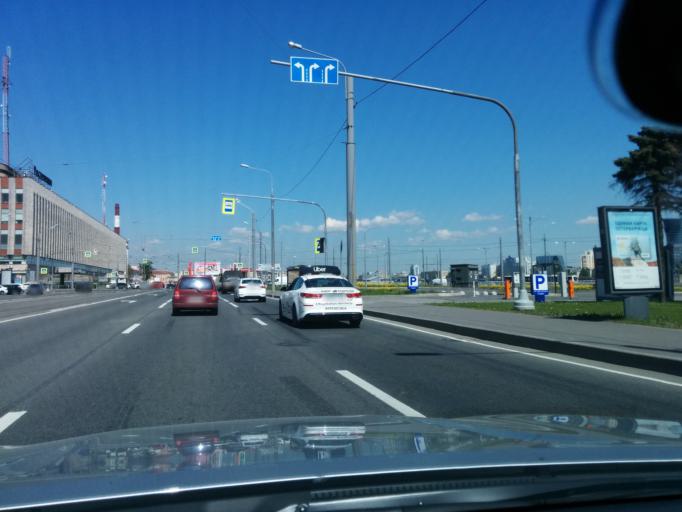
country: RU
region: St.-Petersburg
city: Centralniy
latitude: 59.9254
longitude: 30.3875
